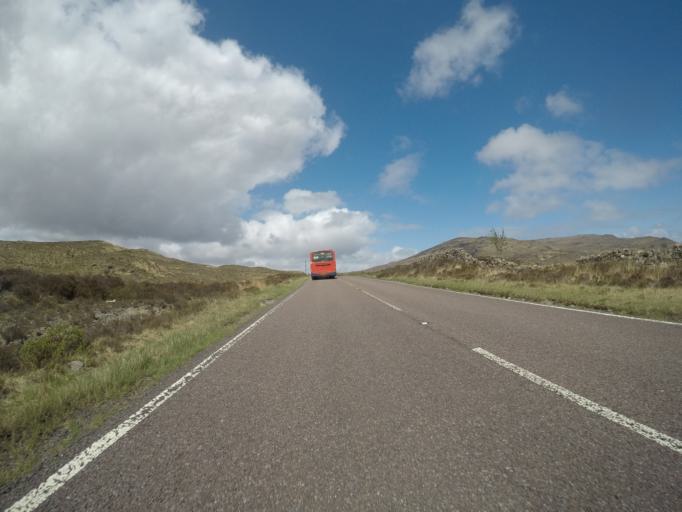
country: GB
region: Scotland
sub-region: Highland
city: Isle of Skye
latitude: 57.2933
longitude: -6.1790
